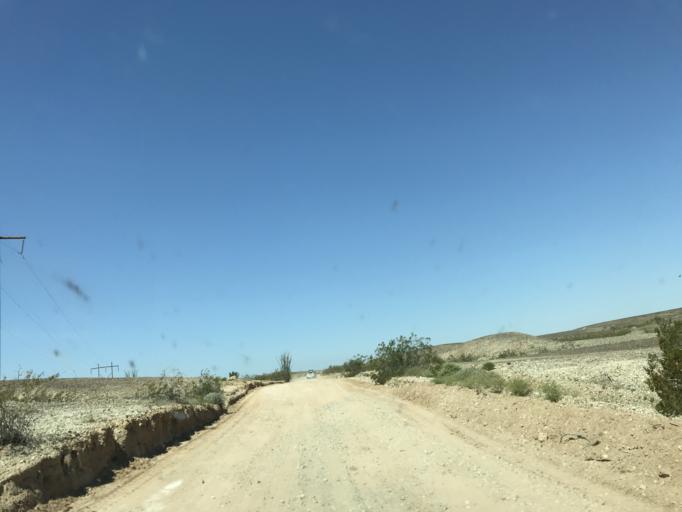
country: US
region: California
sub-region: Riverside County
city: Mesa Verde
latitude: 33.4975
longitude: -114.8448
